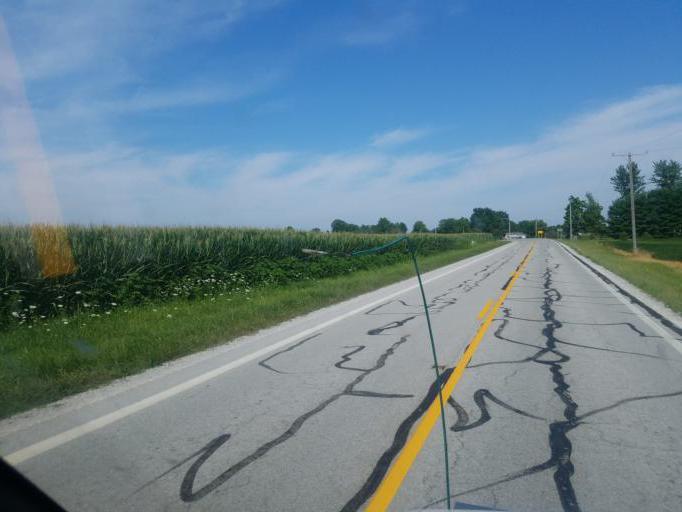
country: US
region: Ohio
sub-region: Logan County
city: Lakeview
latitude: 40.6013
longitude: -83.8868
